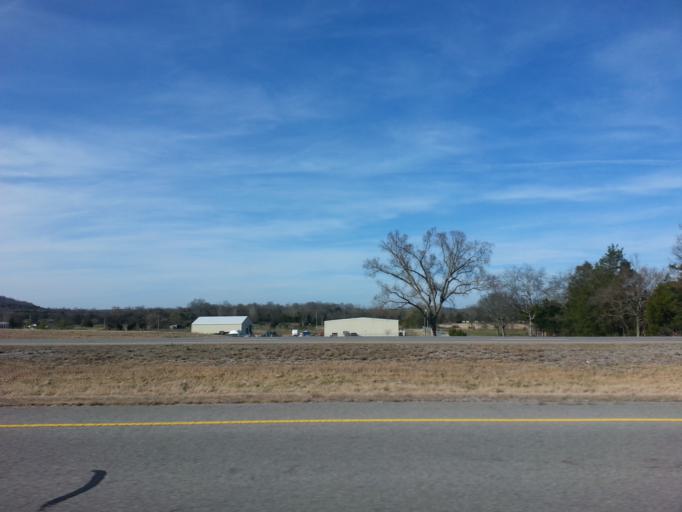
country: US
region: Tennessee
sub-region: Rutherford County
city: Murfreesboro
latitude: 35.8248
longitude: -86.2573
